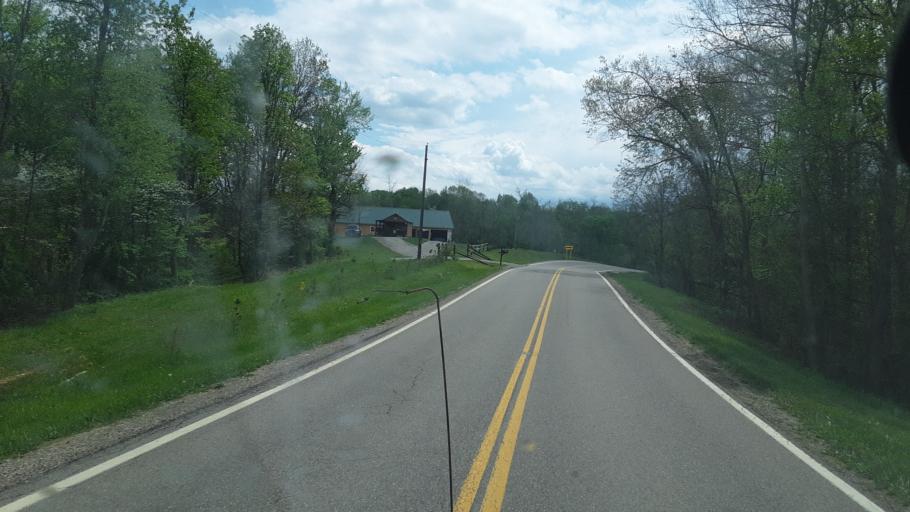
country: US
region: Ohio
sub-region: Noble County
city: Caldwell
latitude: 39.7211
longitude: -81.6572
